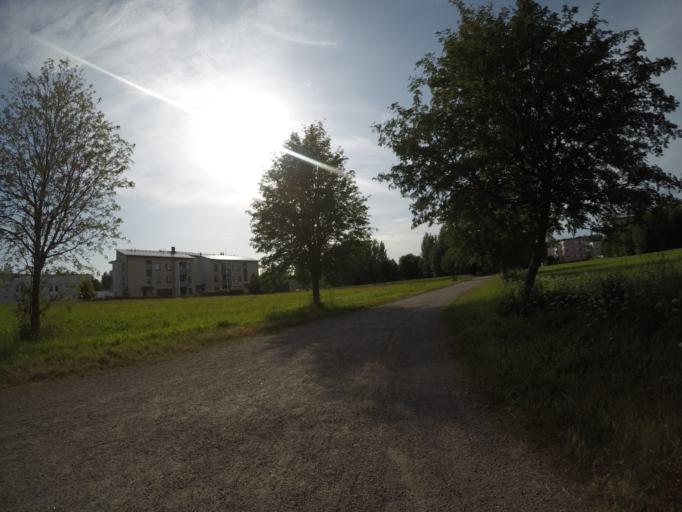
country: FI
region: Haeme
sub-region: Haemeenlinna
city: Haemeenlinna
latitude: 60.9817
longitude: 24.4243
